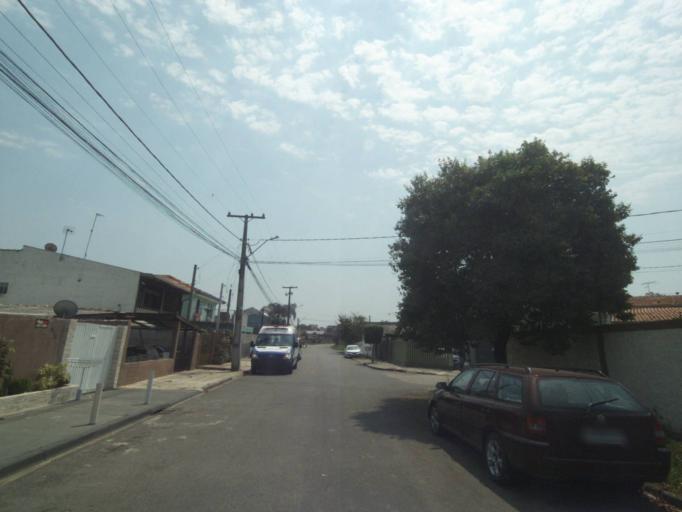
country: BR
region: Parana
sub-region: Sao Jose Dos Pinhais
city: Sao Jose dos Pinhais
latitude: -25.5416
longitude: -49.2453
